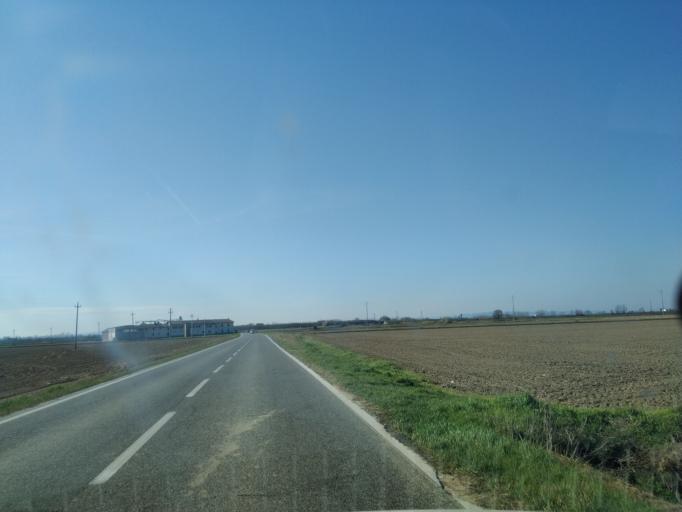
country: IT
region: Piedmont
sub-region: Provincia di Vercelli
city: Asigliano Vercellese
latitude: 45.2811
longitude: 8.4227
